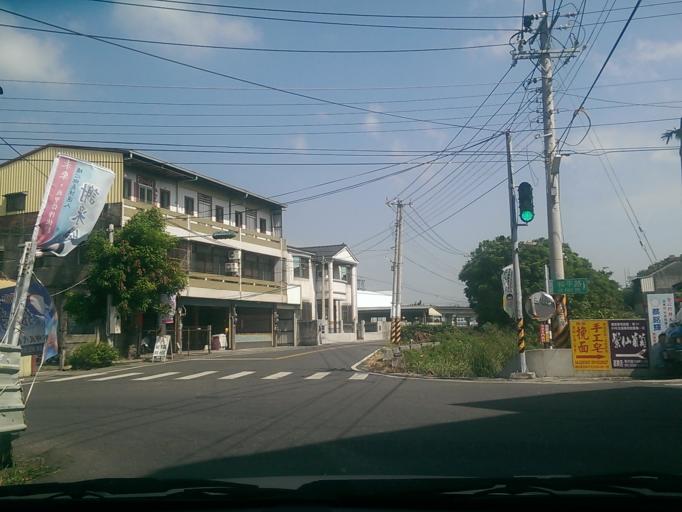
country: TW
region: Taiwan
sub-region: Changhua
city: Chang-hua
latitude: 23.9608
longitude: 120.5443
